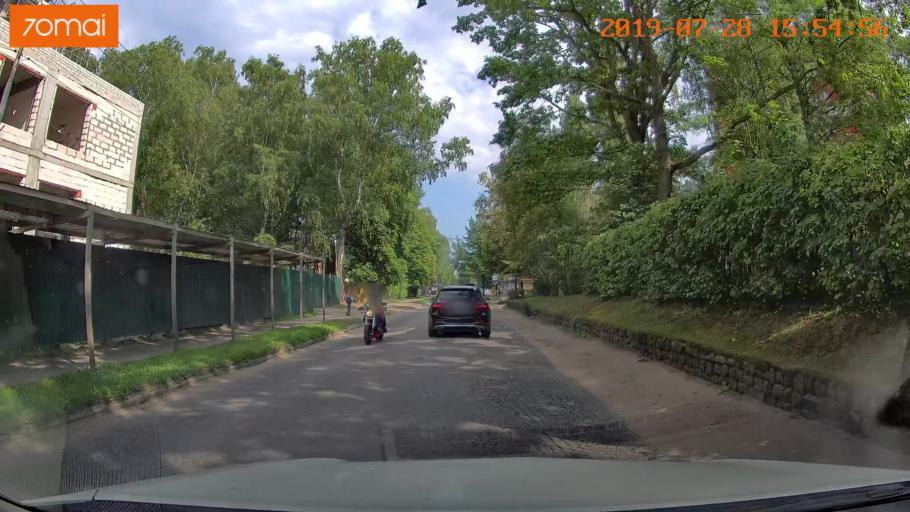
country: RU
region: Kaliningrad
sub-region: Gorod Svetlogorsk
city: Svetlogorsk
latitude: 54.9415
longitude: 20.1371
